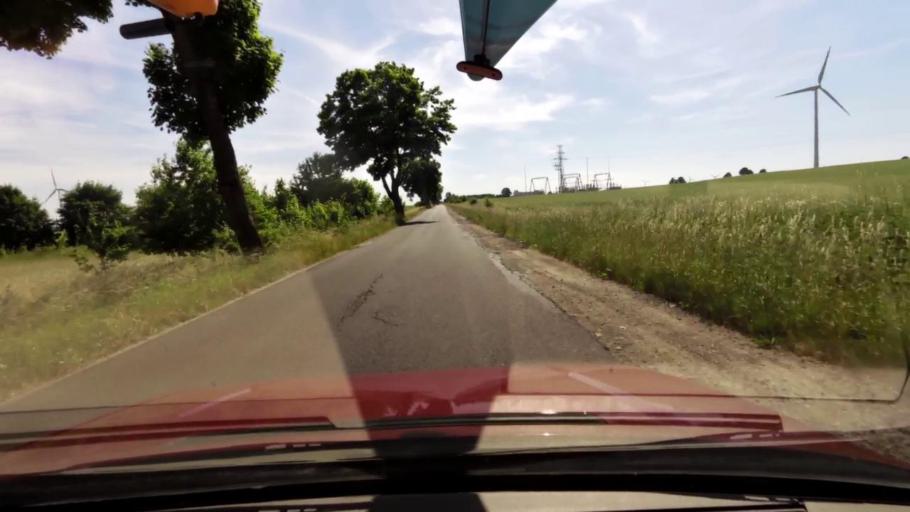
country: PL
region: Pomeranian Voivodeship
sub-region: Powiat slupski
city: Kobylnica
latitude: 54.4032
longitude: 16.9988
